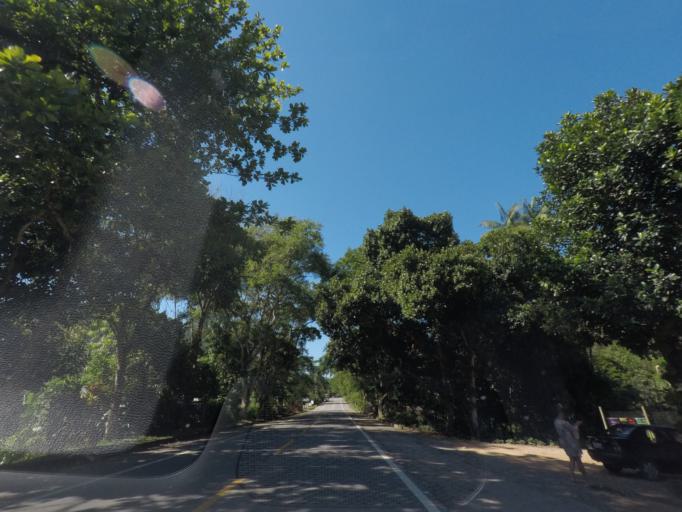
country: BR
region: Rio de Janeiro
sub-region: Parati
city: Paraty
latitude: -23.2783
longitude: -44.6904
